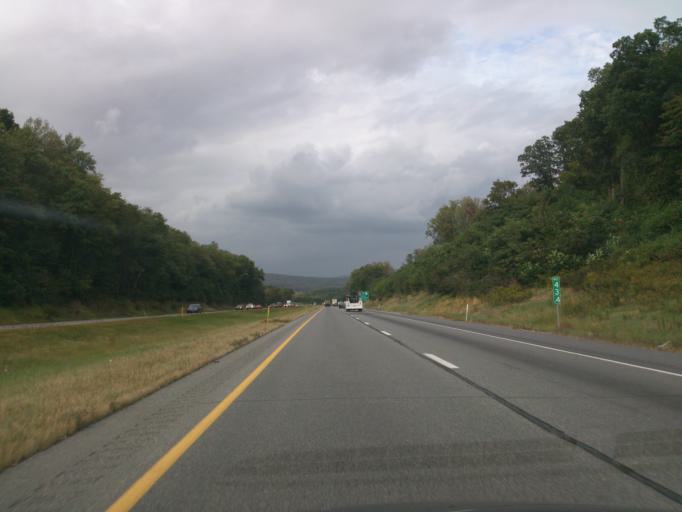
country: US
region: Pennsylvania
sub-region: Lancaster County
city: Reamstown
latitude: 40.1948
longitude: -76.1229
